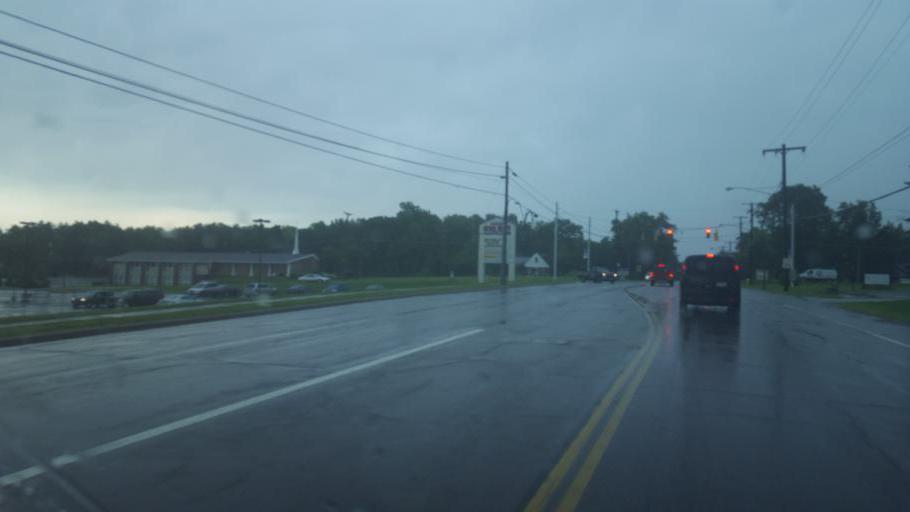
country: US
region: Ohio
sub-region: Richland County
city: Ontario
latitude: 40.7597
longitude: -82.5886
